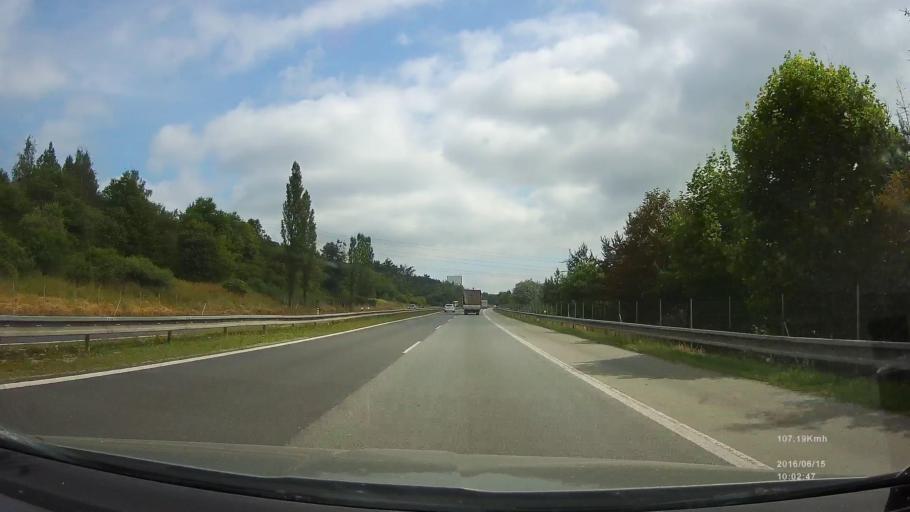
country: SK
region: Kosicky
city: Kosice
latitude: 48.7555
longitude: 21.2799
